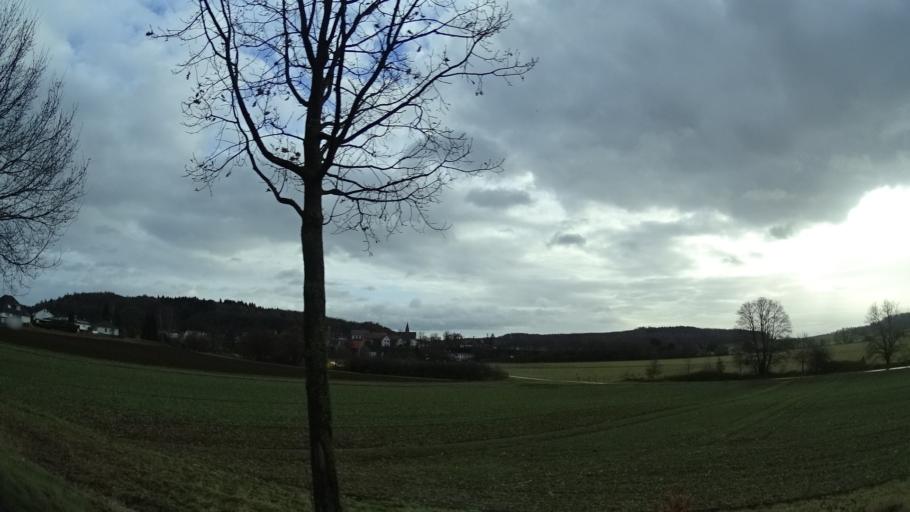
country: DE
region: Hesse
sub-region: Regierungsbezirk Giessen
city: Hungen
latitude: 50.5417
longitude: 8.8982
